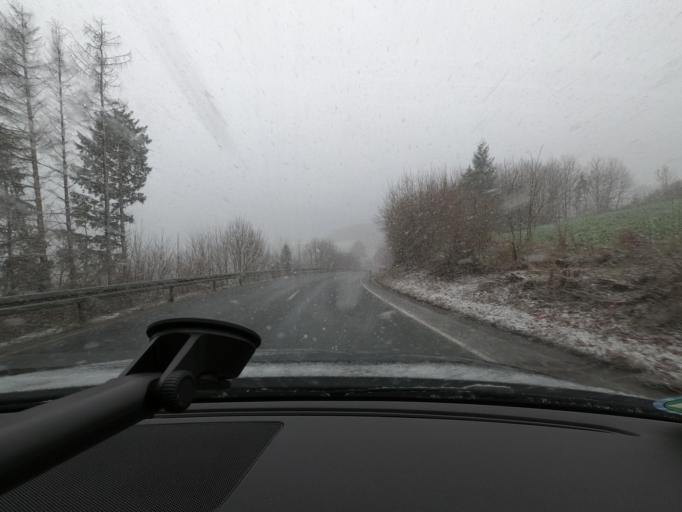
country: DE
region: North Rhine-Westphalia
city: Marsberg
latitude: 51.5065
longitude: 8.8710
